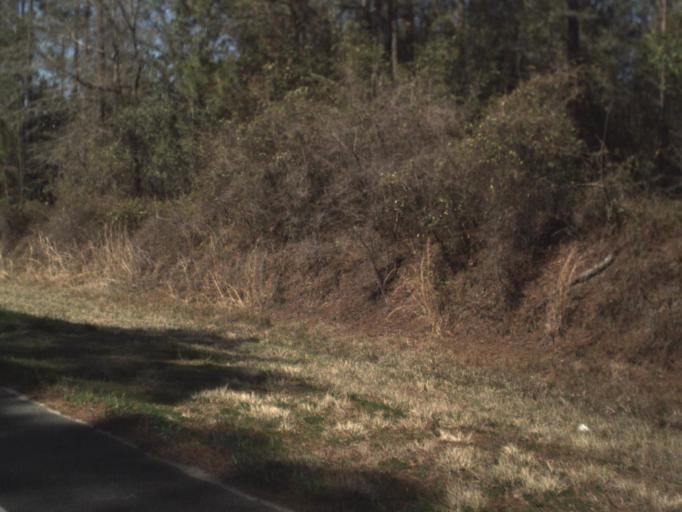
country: US
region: Florida
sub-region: Washington County
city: Chipley
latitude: 30.7911
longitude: -85.3949
